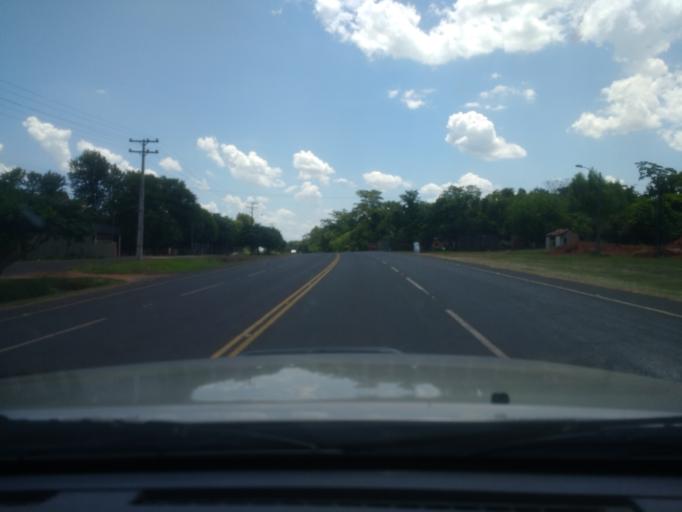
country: PY
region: San Pedro
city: Guayaybi
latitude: -24.5942
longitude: -56.5123
